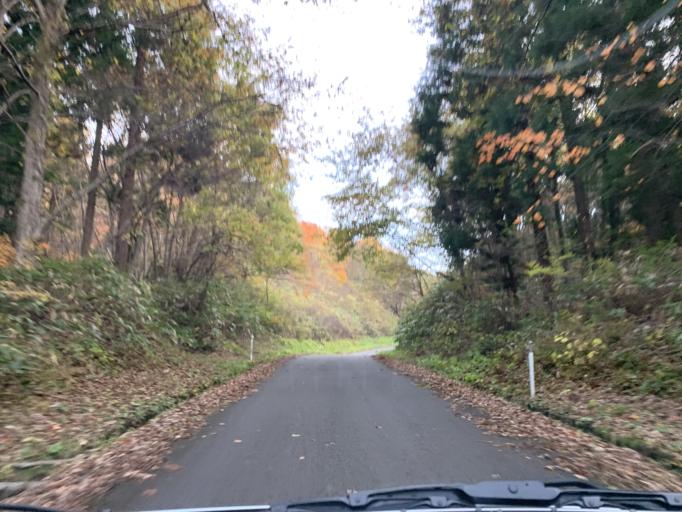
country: JP
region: Iwate
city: Ichinoseki
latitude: 38.9972
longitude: 141.0053
